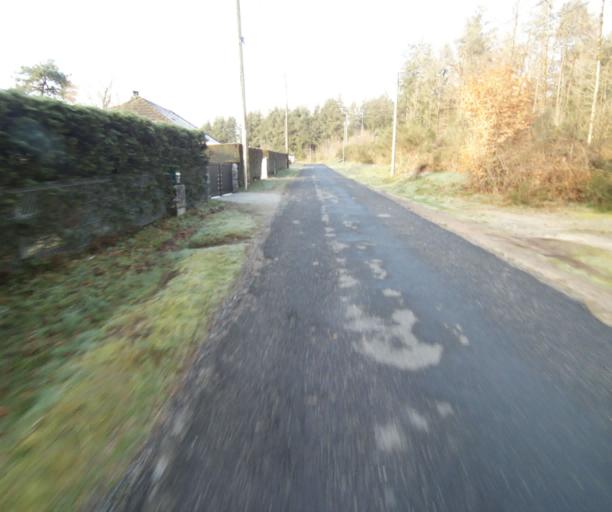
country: FR
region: Limousin
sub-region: Departement de la Correze
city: Correze
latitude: 45.3248
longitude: 1.8659
